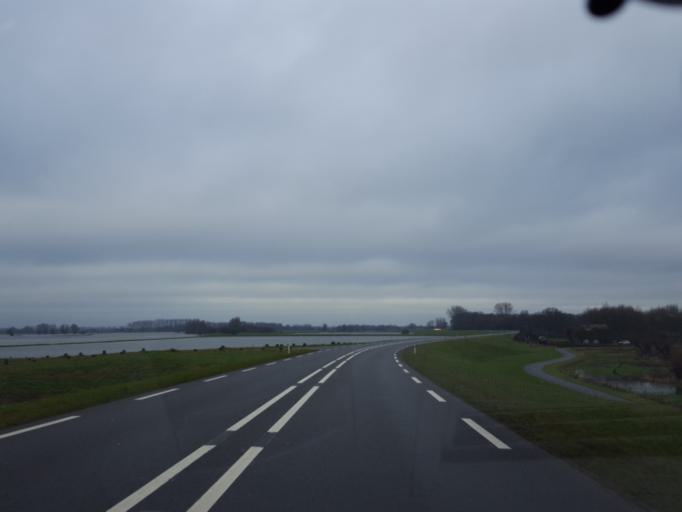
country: NL
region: Overijssel
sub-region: Gemeente Olst-Wijhe
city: Olst
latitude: 52.3082
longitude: 6.1091
